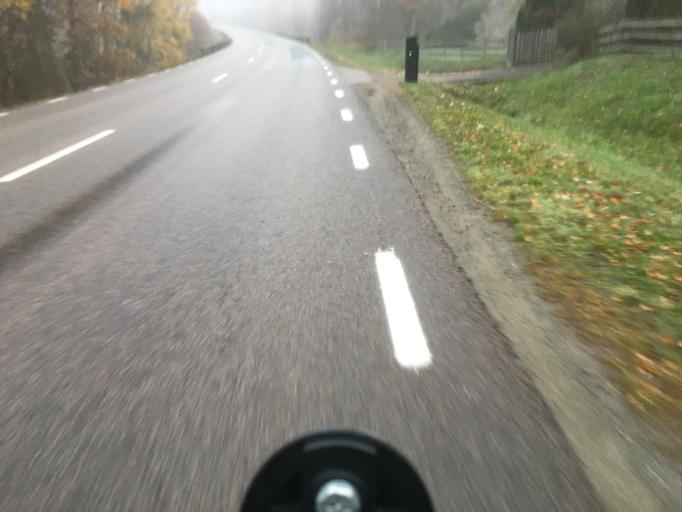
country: SE
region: Blekinge
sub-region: Karlshamns Kommun
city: Morrum
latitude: 56.1852
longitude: 14.7679
